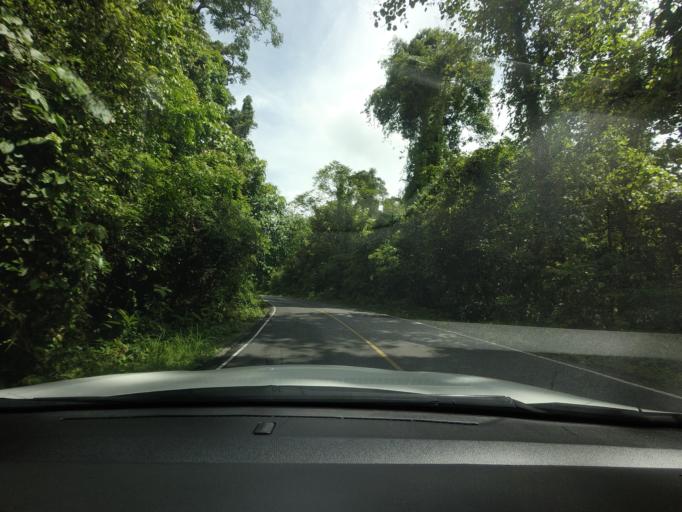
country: TH
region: Nakhon Nayok
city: Pak Phli
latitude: 14.3161
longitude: 101.3783
